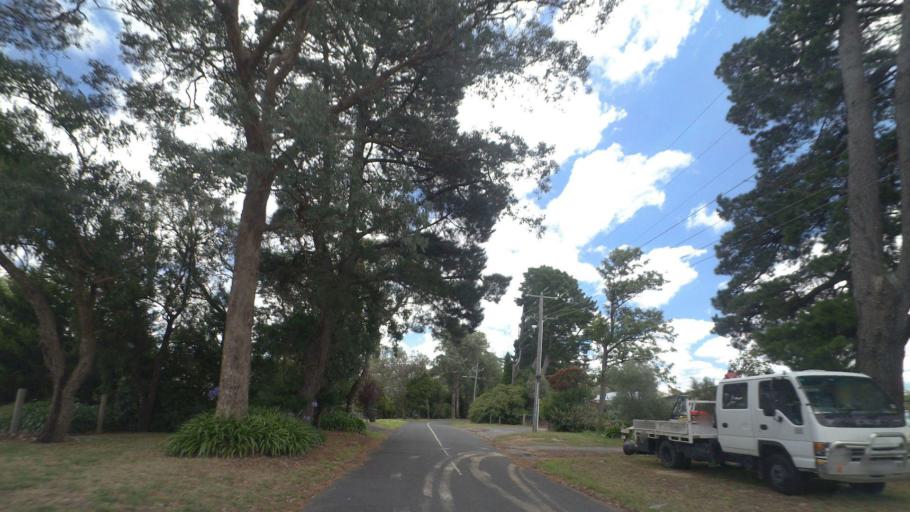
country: AU
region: Victoria
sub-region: Maroondah
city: Croydon Hills
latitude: -37.7657
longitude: 145.2650
